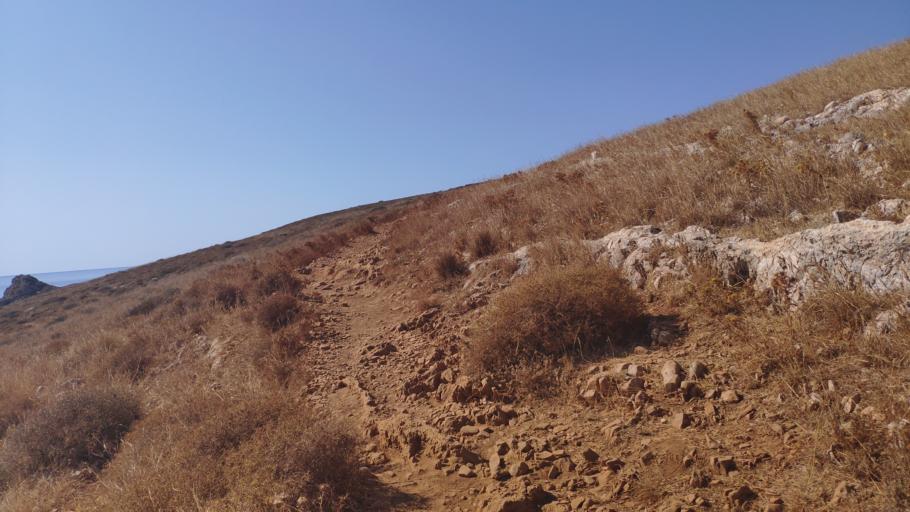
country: GR
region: Peloponnese
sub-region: Nomos Lakonias
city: Gytheio
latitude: 36.3978
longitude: 22.4850
